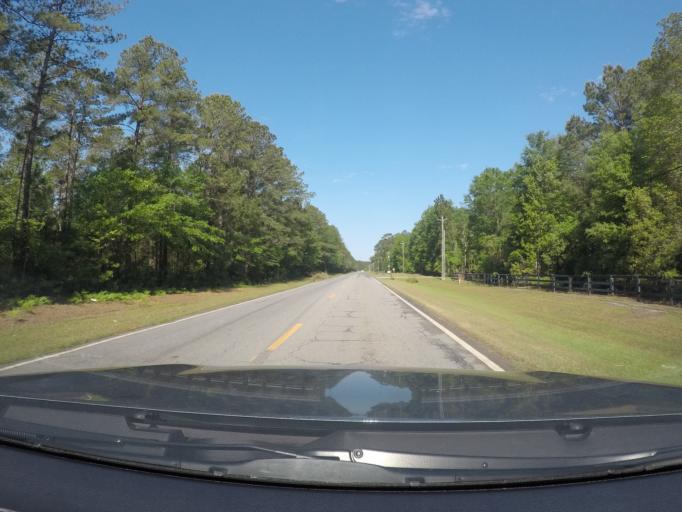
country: US
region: Georgia
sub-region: Chatham County
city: Bloomingdale
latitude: 32.0568
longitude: -81.3023
